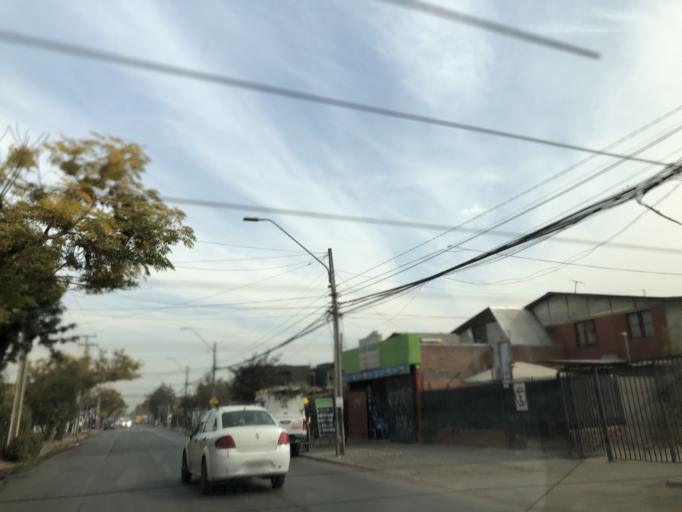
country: CL
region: Santiago Metropolitan
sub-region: Provincia de Cordillera
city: Puente Alto
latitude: -33.5677
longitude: -70.5680
